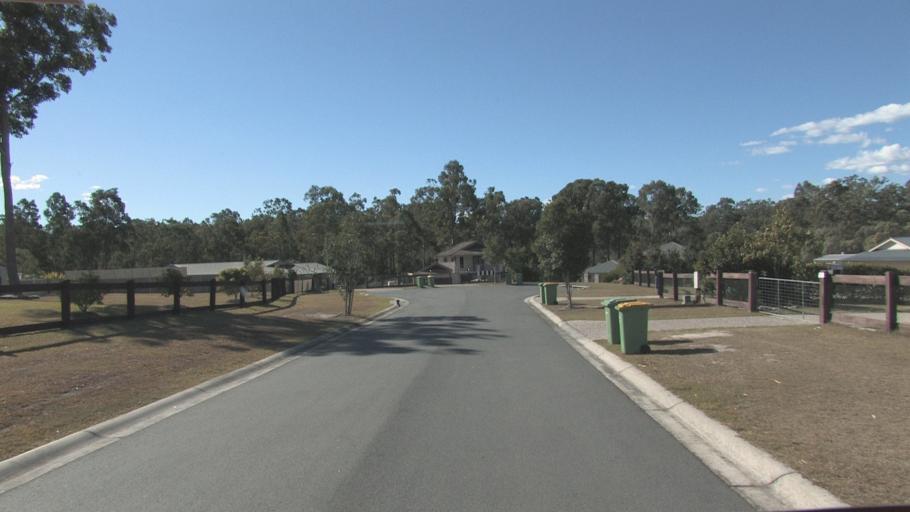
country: AU
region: Queensland
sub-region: Ipswich
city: Springfield Lakes
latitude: -27.7307
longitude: 152.9168
